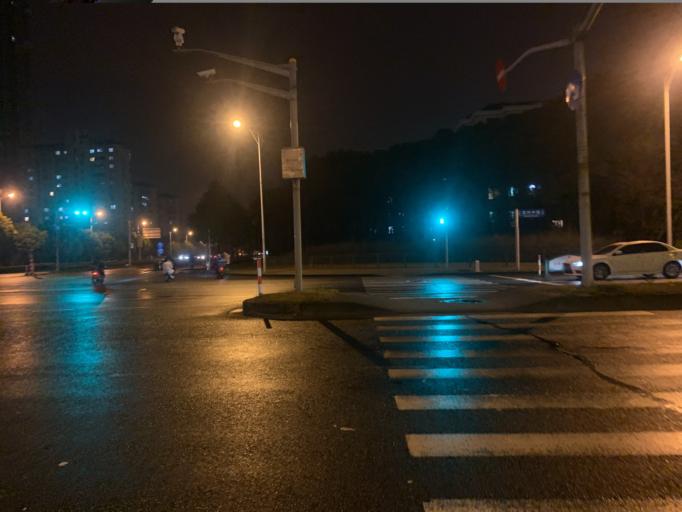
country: CN
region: Shanghai Shi
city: Huamu
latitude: 31.2054
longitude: 121.6302
